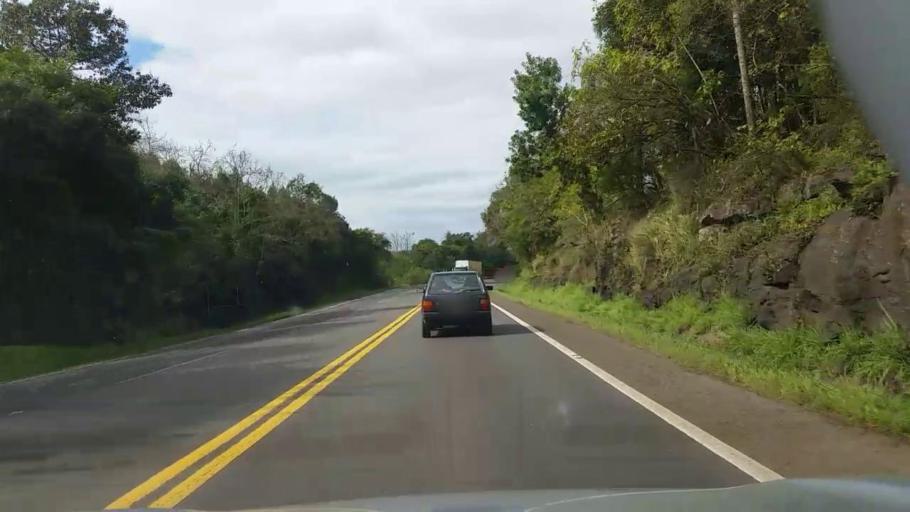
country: BR
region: Rio Grande do Sul
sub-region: Arroio Do Meio
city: Arroio do Meio
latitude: -29.3877
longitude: -52.0461
